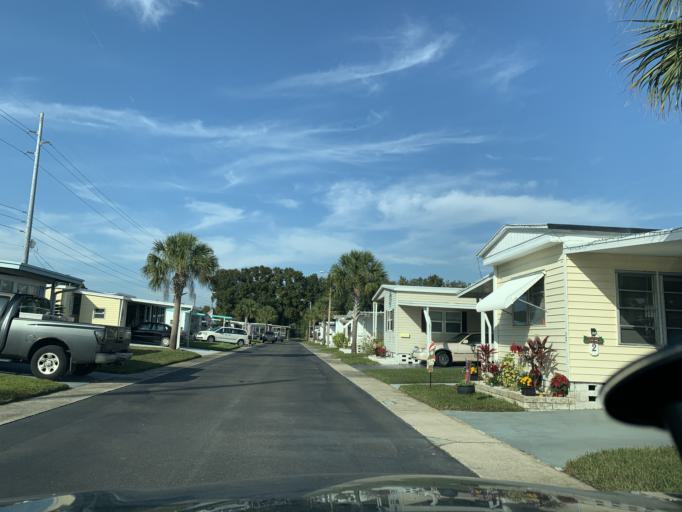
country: US
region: Florida
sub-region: Pinellas County
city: Largo
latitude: 27.8980
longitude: -82.7828
